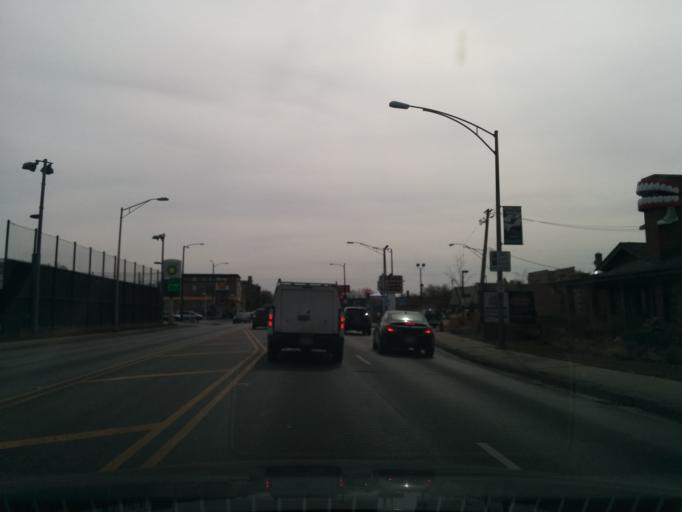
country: US
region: Illinois
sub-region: Cook County
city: Forest Park
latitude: 41.8661
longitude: -87.8043
